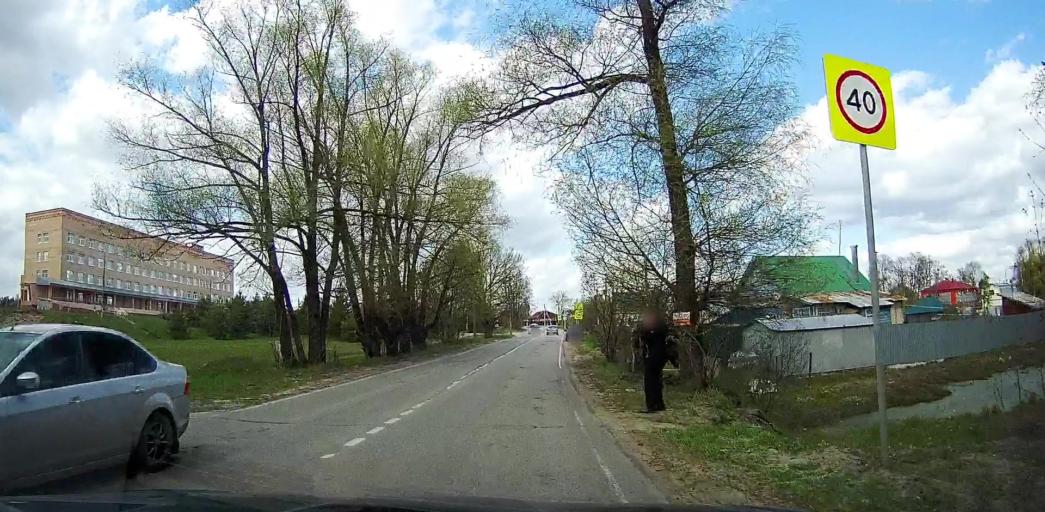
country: RU
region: Moskovskaya
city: Davydovo
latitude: 55.6079
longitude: 38.8476
